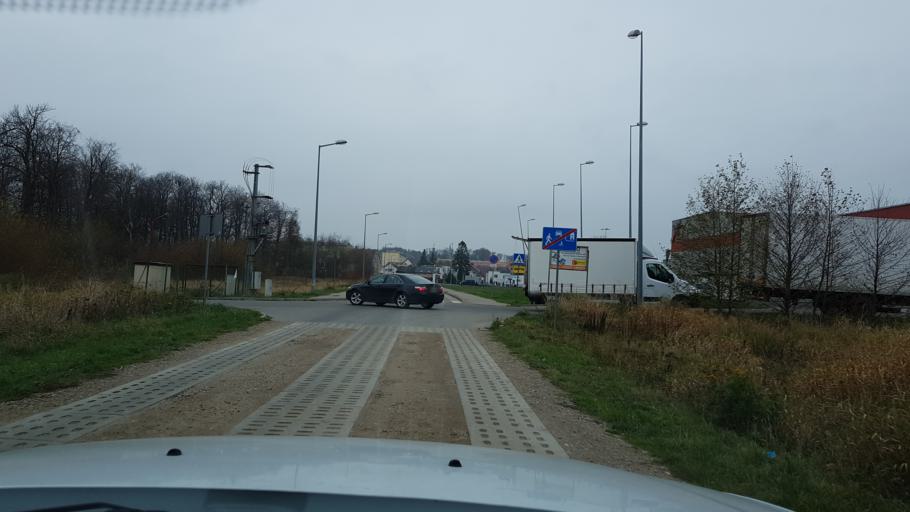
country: PL
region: West Pomeranian Voivodeship
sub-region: Powiat slawienski
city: Darlowo
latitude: 54.4172
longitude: 16.4162
